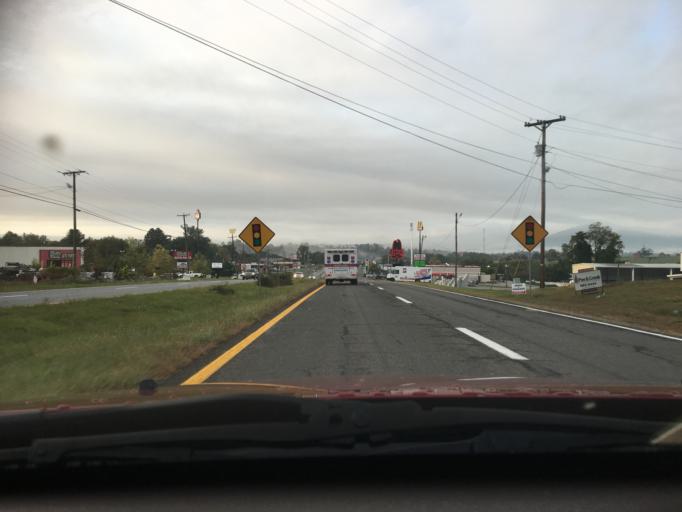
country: US
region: Virginia
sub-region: Pulaski County
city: Dublin
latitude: 37.0866
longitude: -80.6893
